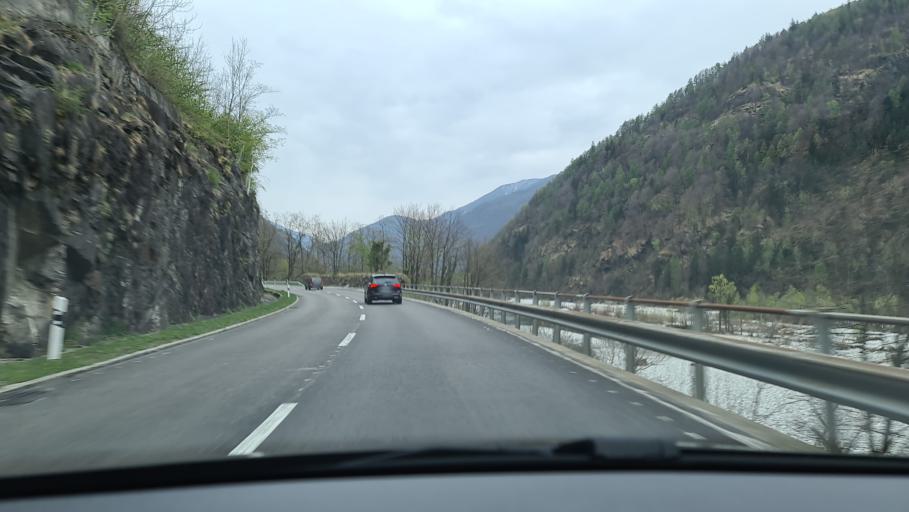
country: CH
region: Ticino
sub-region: Vallemaggia District
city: Cevio
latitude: 46.2764
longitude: 8.6743
